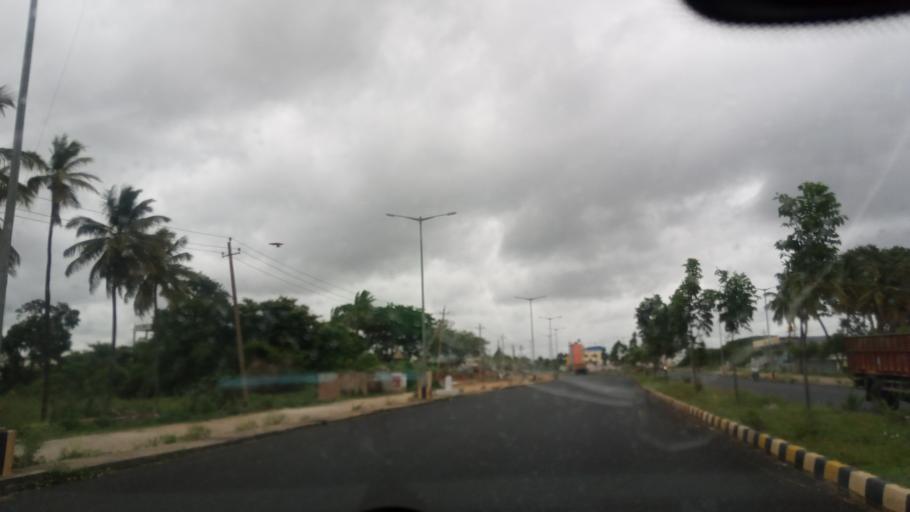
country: IN
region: Karnataka
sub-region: Mysore
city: Mysore
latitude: 12.2865
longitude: 76.6082
